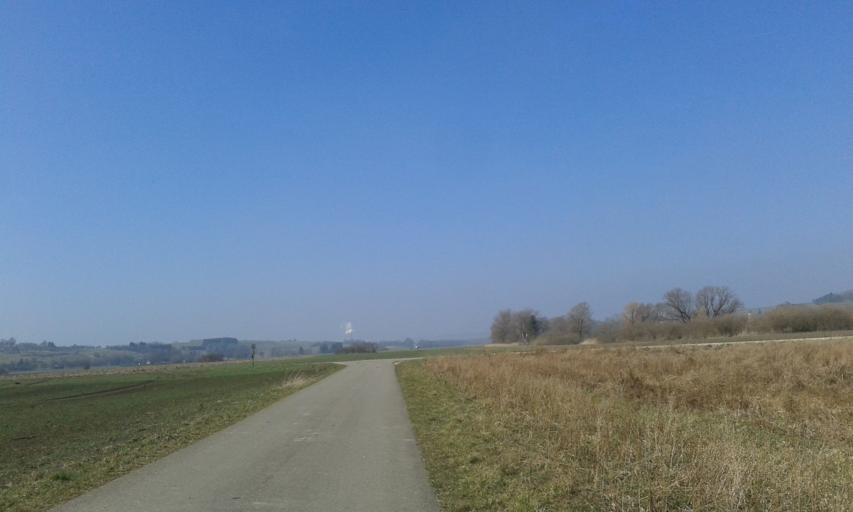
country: DE
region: Baden-Wuerttemberg
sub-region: Tuebingen Region
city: Griesingen
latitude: 48.2752
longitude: 9.7884
